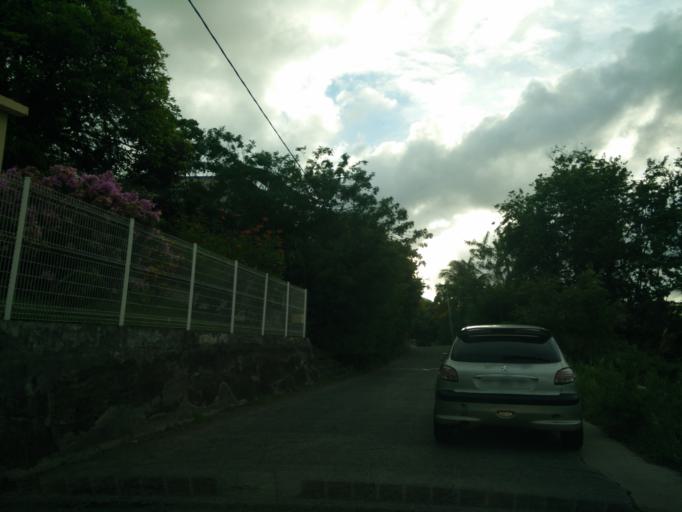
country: MQ
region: Martinique
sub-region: Martinique
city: Le Marin
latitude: 14.4598
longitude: -60.8444
